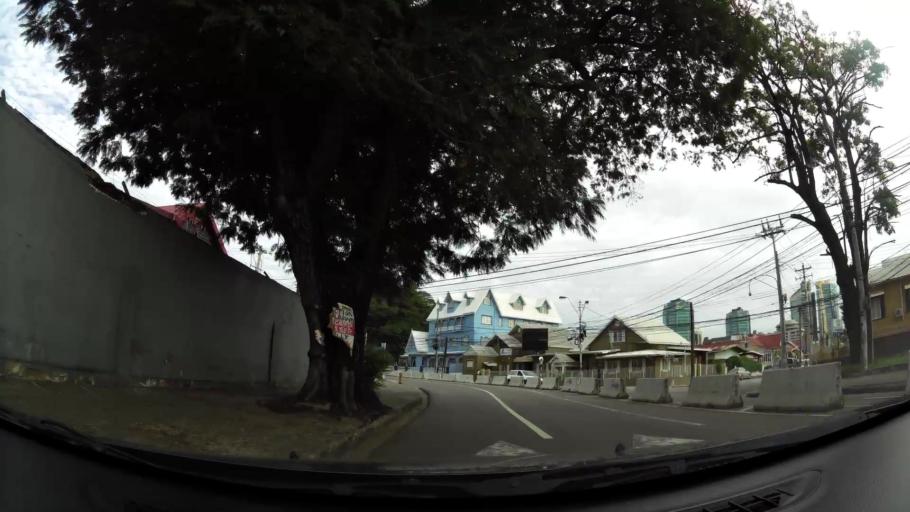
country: TT
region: City of Port of Spain
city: Port-of-Spain
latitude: 10.6567
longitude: -61.5167
